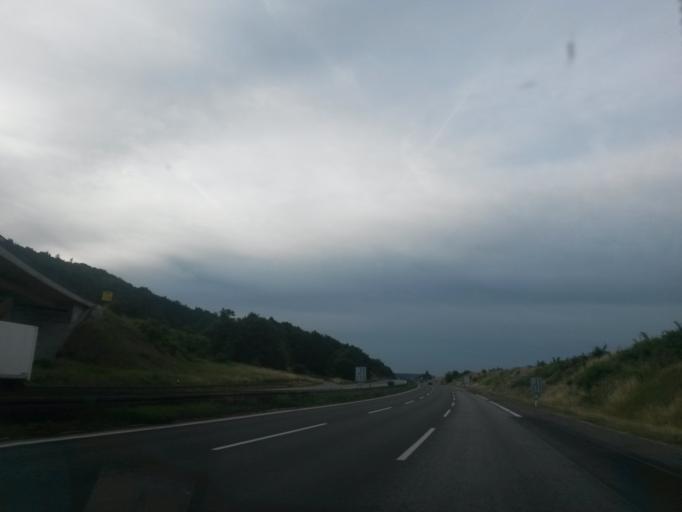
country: DE
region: Bavaria
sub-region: Regierungsbezirk Mittelfranken
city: Greding
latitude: 49.0748
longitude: 11.2964
